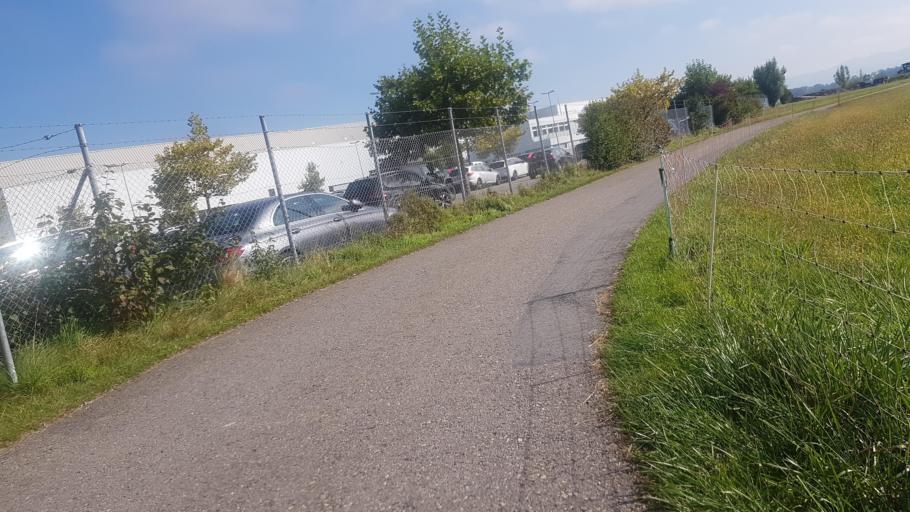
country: CH
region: Appenzell Ausserrhoden
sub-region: Bezirk Vorderland
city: Heiden
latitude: 47.4873
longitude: 9.5468
